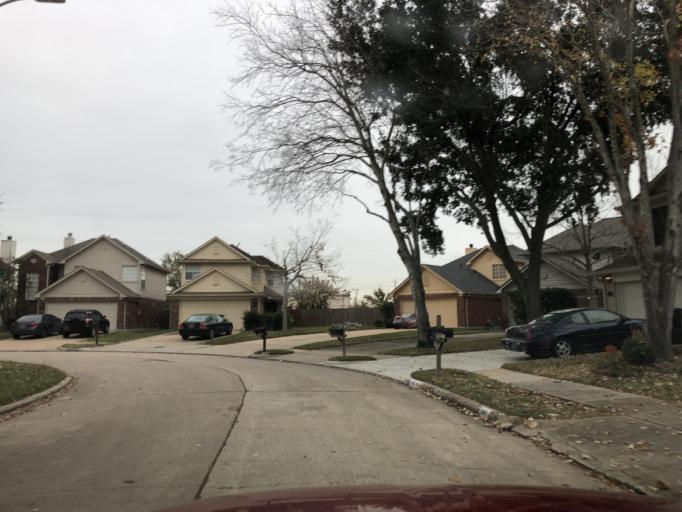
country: US
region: Texas
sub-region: Fort Bend County
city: Missouri City
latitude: 29.6401
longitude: -95.5290
